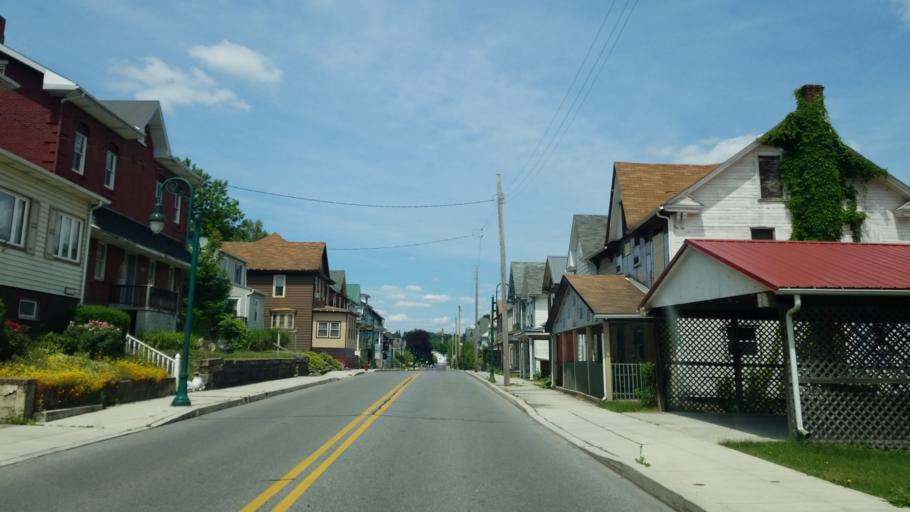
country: US
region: Pennsylvania
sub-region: Blair County
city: Tyrone
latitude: 40.6673
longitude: -78.2449
